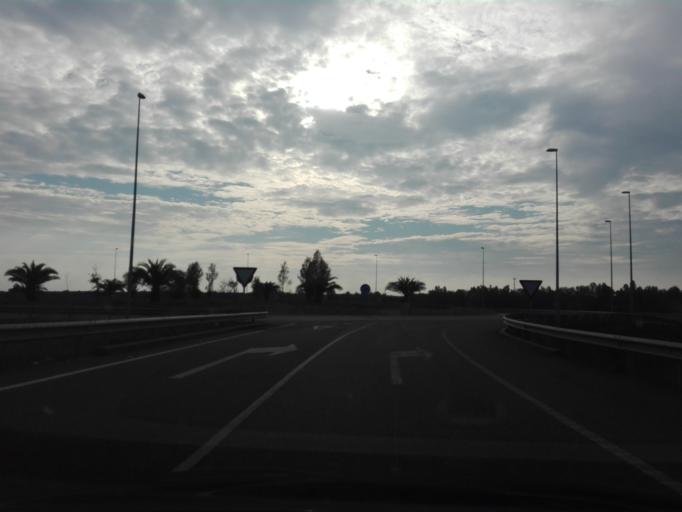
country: ES
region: Extremadura
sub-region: Provincia de Badajoz
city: Badajoz
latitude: 38.9213
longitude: -6.9475
